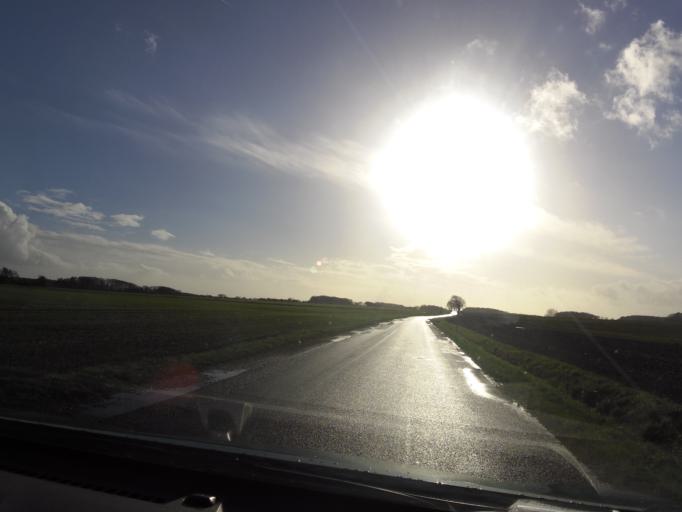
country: DK
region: Central Jutland
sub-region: Odder Kommune
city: Odder
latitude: 55.8820
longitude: 10.1711
